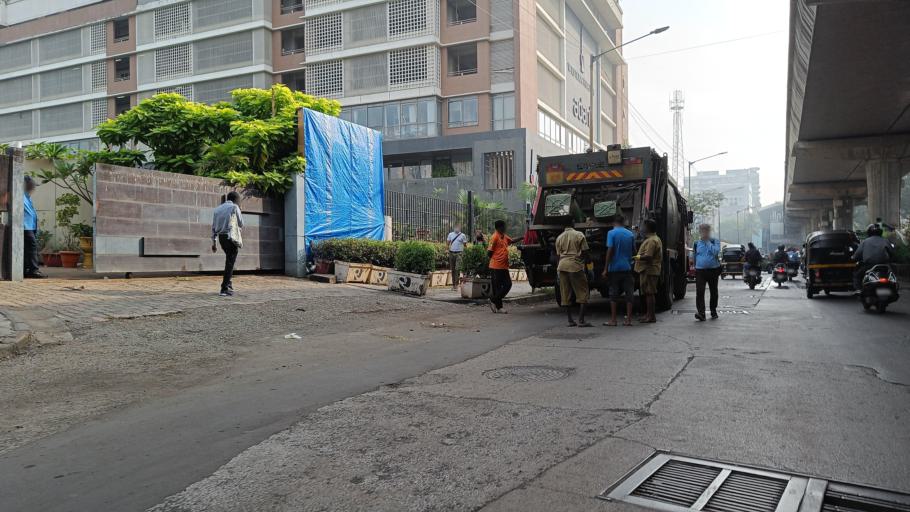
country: IN
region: Maharashtra
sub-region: Mumbai Suburban
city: Powai
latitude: 19.1289
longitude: 72.8269
